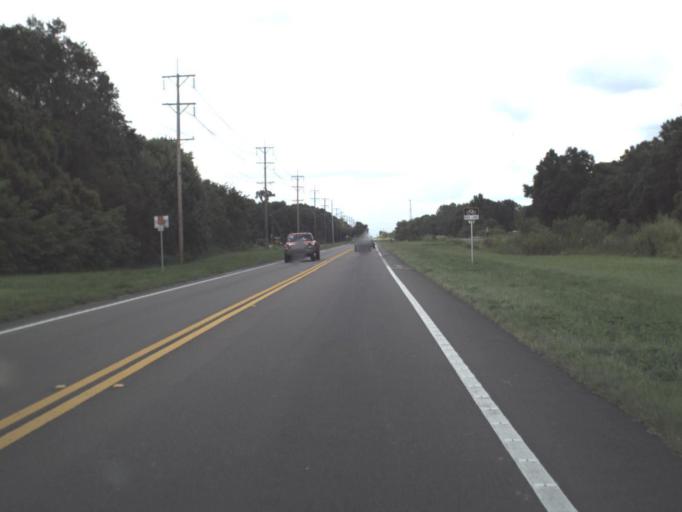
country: US
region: Florida
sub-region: Hillsborough County
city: Plant City
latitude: 28.0861
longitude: -82.1397
